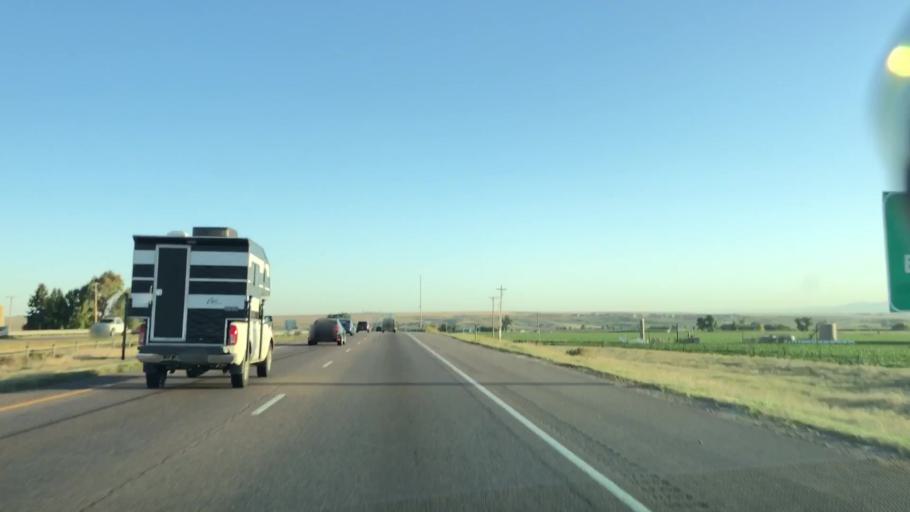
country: US
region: Colorado
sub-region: Weld County
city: Johnstown
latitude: 40.3226
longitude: -104.9805
